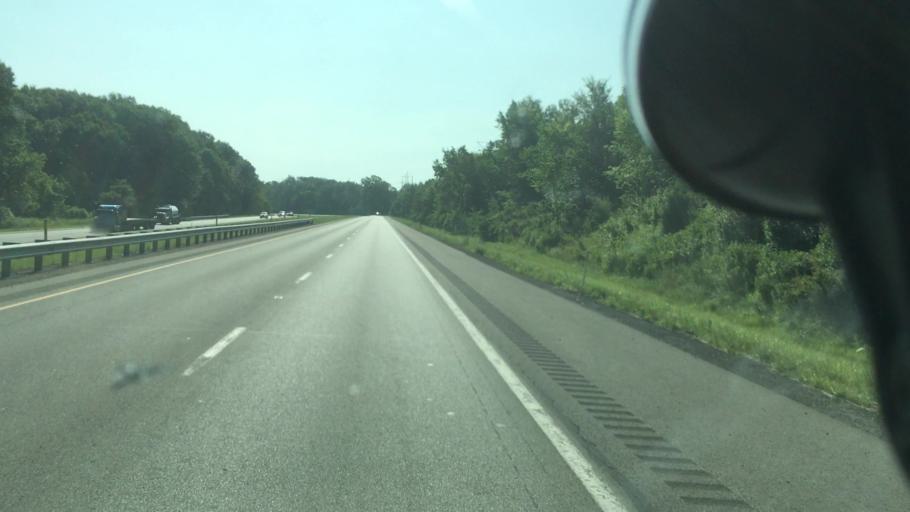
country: US
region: Pennsylvania
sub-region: Lawrence County
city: New Castle
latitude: 40.9680
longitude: -80.3340
